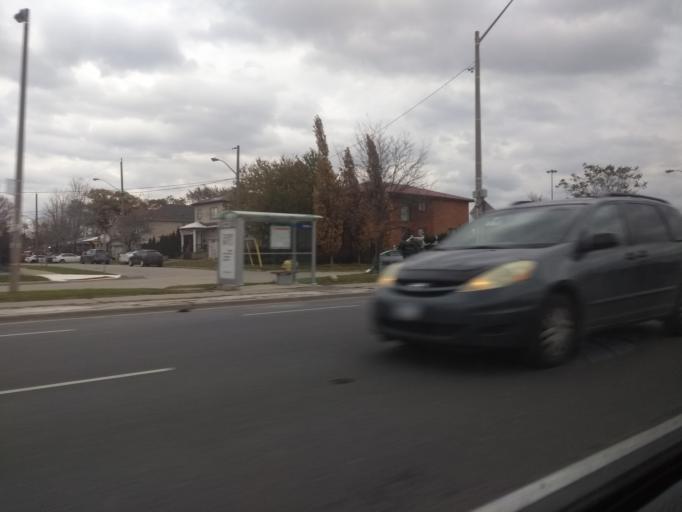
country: CA
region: Ontario
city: Etobicoke
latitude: 43.7137
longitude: -79.5067
